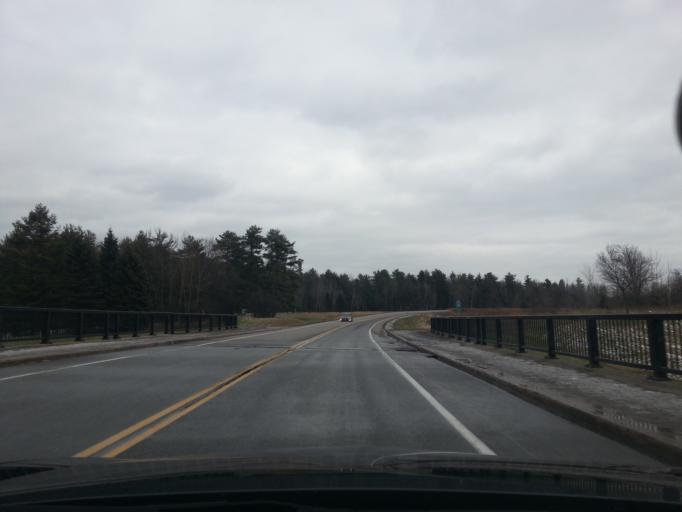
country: CA
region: Quebec
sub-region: Outaouais
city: Gatineau
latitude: 45.4706
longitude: -75.5733
